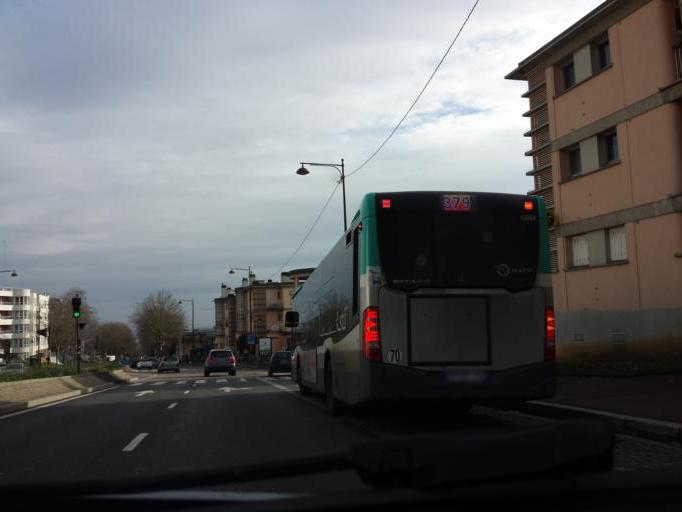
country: FR
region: Ile-de-France
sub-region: Departement des Hauts-de-Seine
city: Chatenay-Malabry
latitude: 48.7655
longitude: 2.2597
